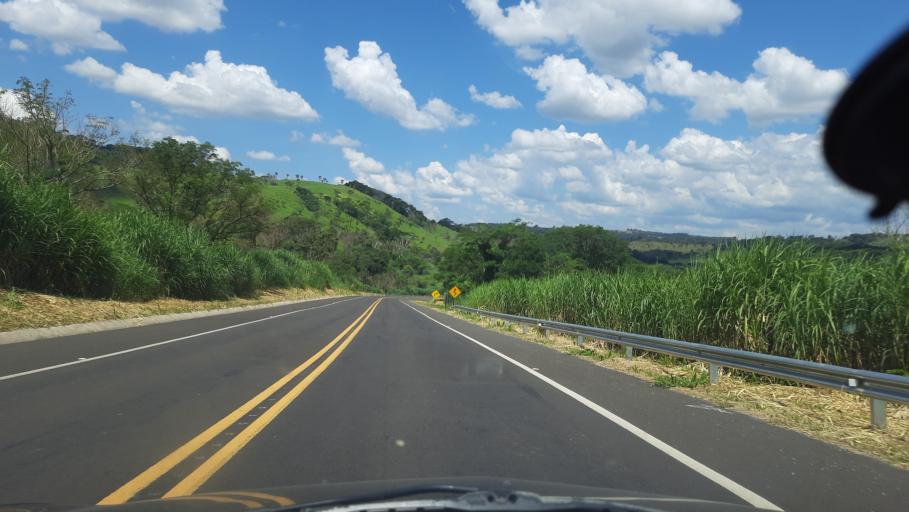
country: BR
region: Sao Paulo
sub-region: Sao Jose Do Rio Pardo
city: Sao Jose do Rio Pardo
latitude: -21.6040
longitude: -46.9751
